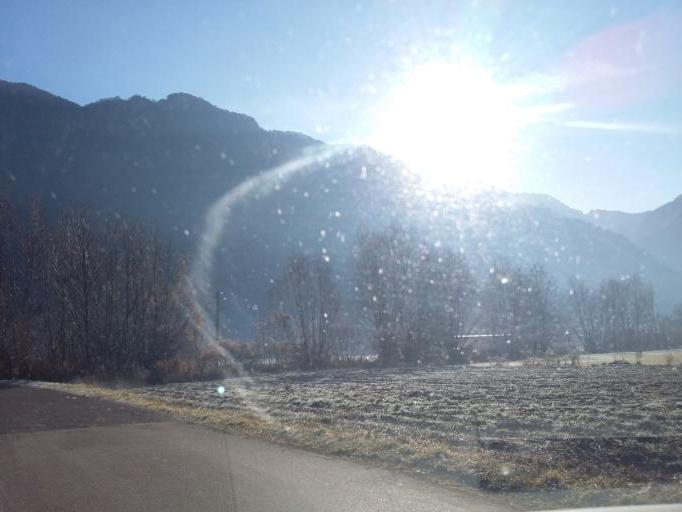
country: IT
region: Trentino-Alto Adige
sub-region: Provincia di Trento
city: Lodrone-Darzo
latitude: 45.8216
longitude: 10.5451
